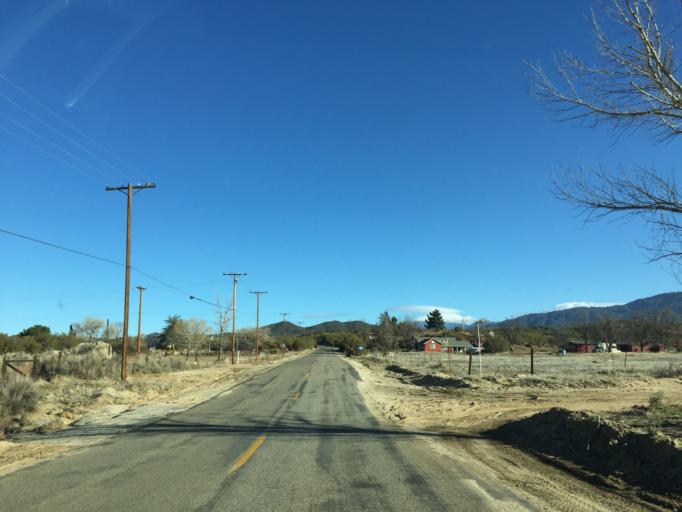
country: US
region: California
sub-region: Riverside County
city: Anza
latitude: 33.5653
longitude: -116.7360
